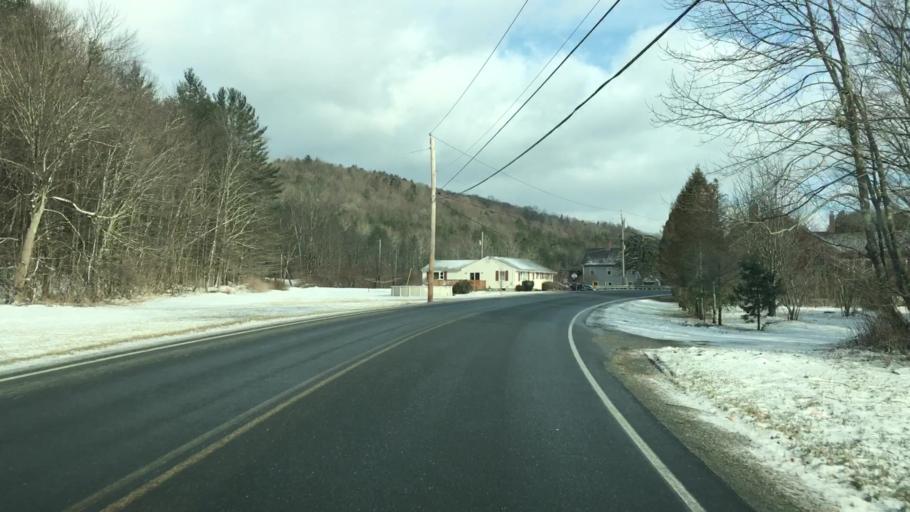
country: US
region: Massachusetts
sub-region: Franklin County
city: Colrain
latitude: 42.7078
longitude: -72.7025
